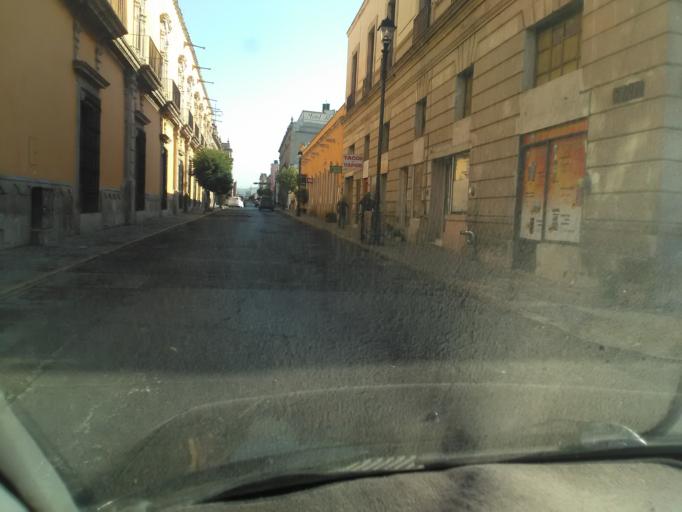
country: MX
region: Durango
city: Victoria de Durango
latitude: 24.0232
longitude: -104.6712
